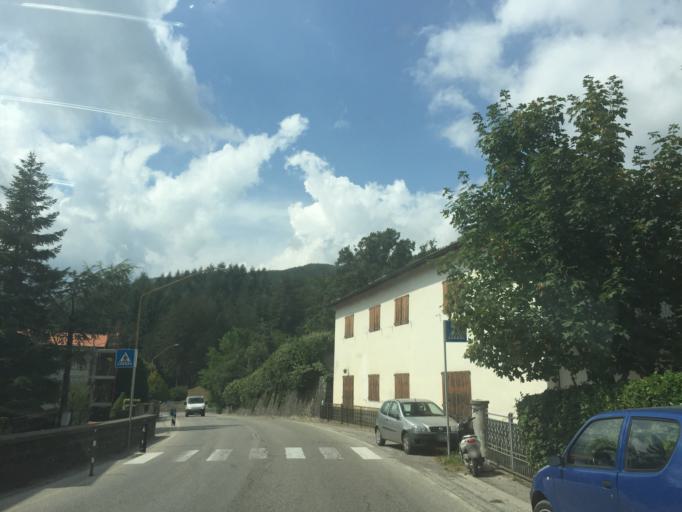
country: IT
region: Tuscany
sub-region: Provincia di Pistoia
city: San Marcello Pistoiese
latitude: 44.0549
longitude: 10.7993
